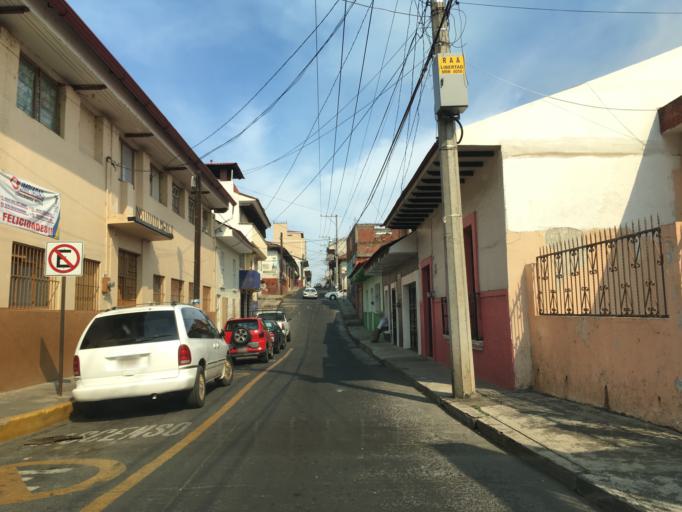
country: MX
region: Michoacan
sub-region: Uruapan
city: Uruapan
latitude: 19.4192
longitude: -102.0651
